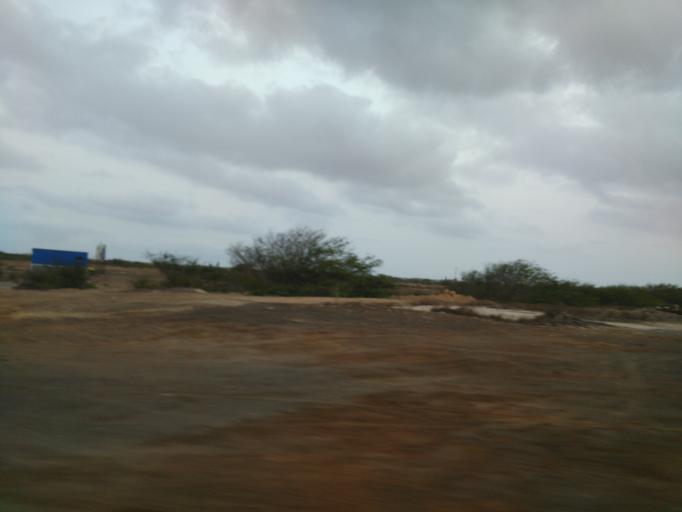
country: CV
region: Sal
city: Santa Maria
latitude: 16.6663
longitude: -22.9329
